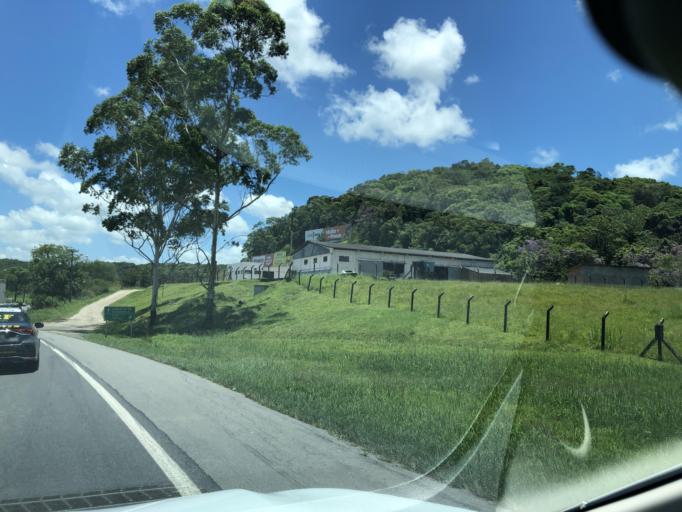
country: BR
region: Santa Catarina
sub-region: Joinville
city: Joinville
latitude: -26.4340
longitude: -48.8042
